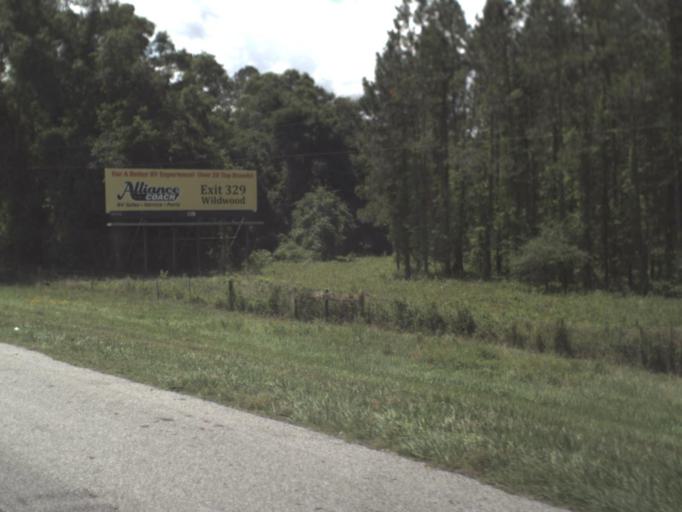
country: US
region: Florida
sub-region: Suwannee County
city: Wellborn
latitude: 30.3057
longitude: -82.7950
